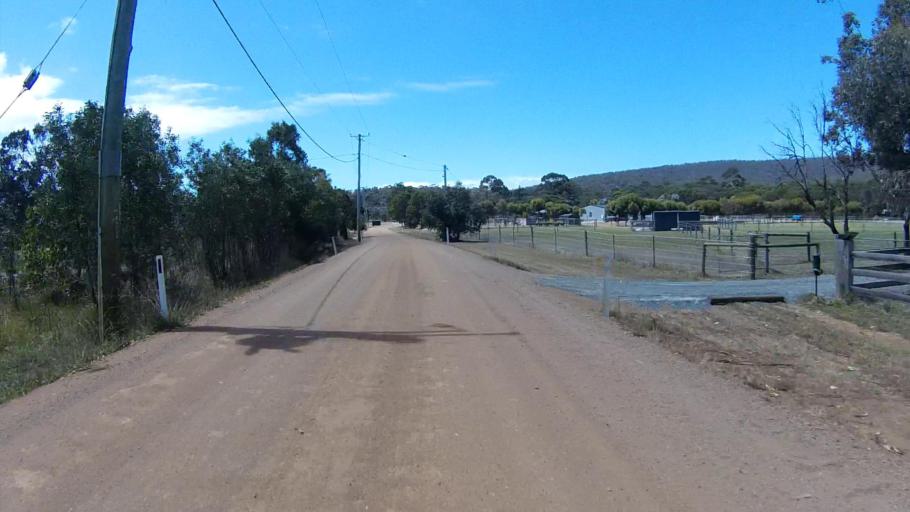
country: AU
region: Tasmania
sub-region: Clarence
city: Sandford
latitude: -42.9652
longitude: 147.4716
